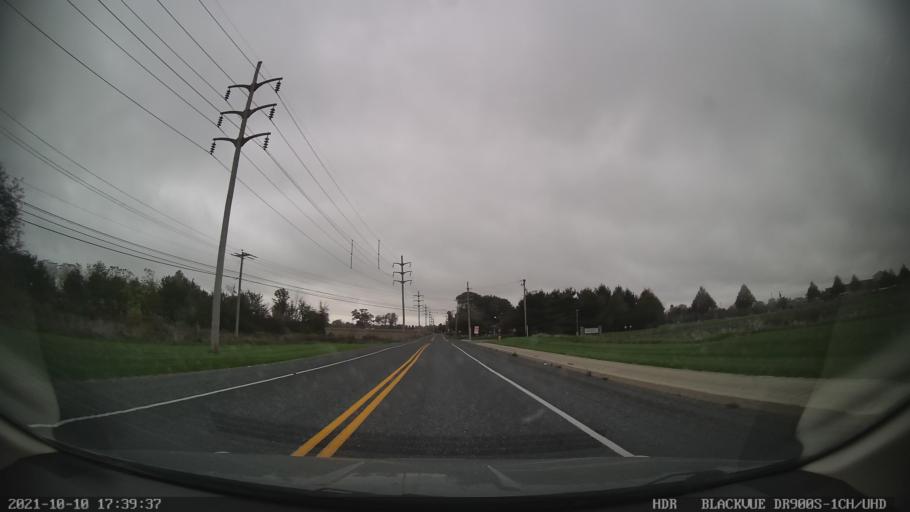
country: US
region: Pennsylvania
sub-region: Berks County
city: Topton
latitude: 40.5095
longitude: -75.6967
